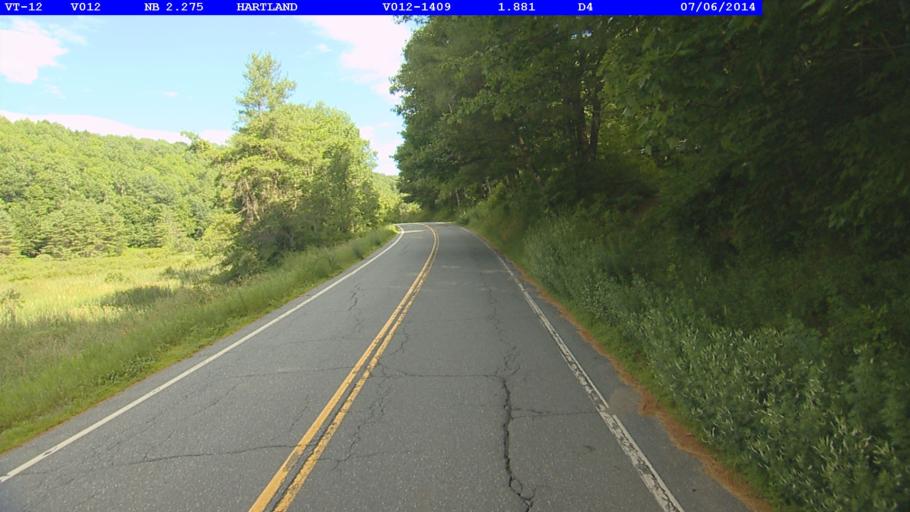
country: US
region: Vermont
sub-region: Windsor County
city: Windsor
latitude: 43.5483
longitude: -72.4327
